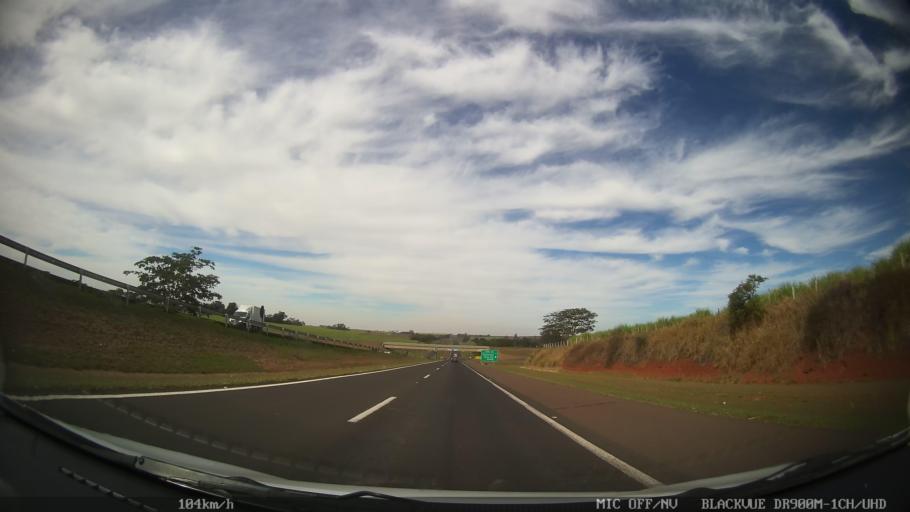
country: BR
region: Sao Paulo
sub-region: Taquaritinga
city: Taquaritinga
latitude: -21.5143
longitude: -48.5425
